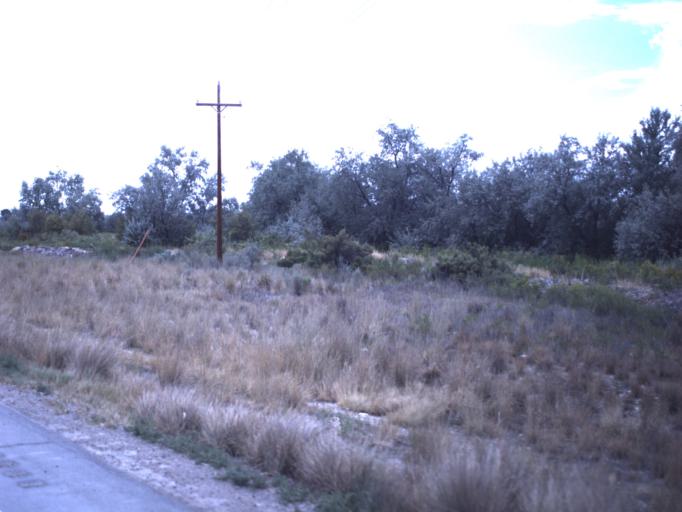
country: US
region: Utah
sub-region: Duchesne County
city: Roosevelt
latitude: 40.1931
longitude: -110.0759
